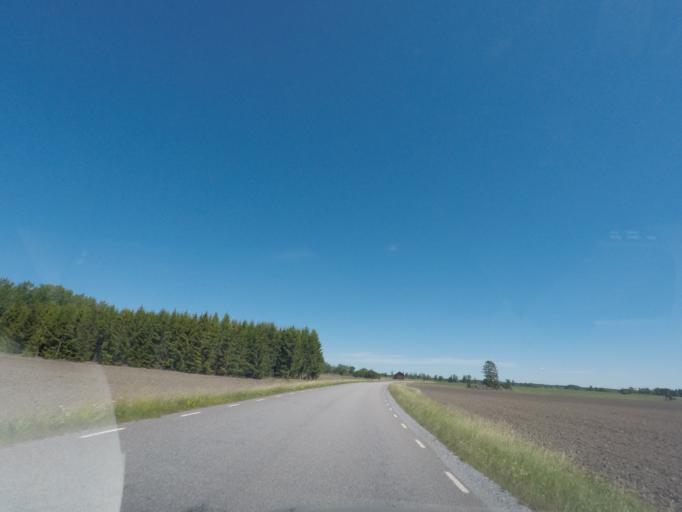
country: SE
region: Uppsala
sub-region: Enkopings Kommun
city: Irsta
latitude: 59.6802
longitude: 16.9500
